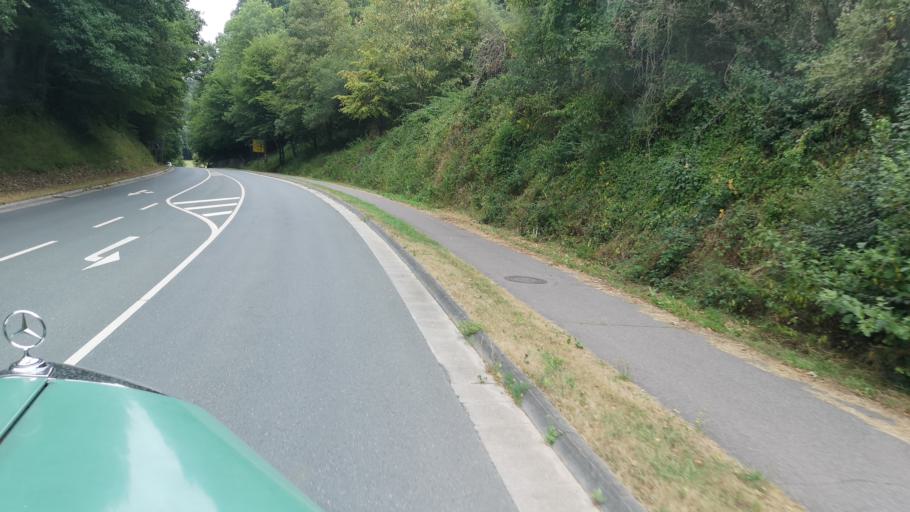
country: DE
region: North Rhine-Westphalia
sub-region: Regierungsbezirk Koln
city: Odenthal
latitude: 51.0545
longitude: 7.1356
